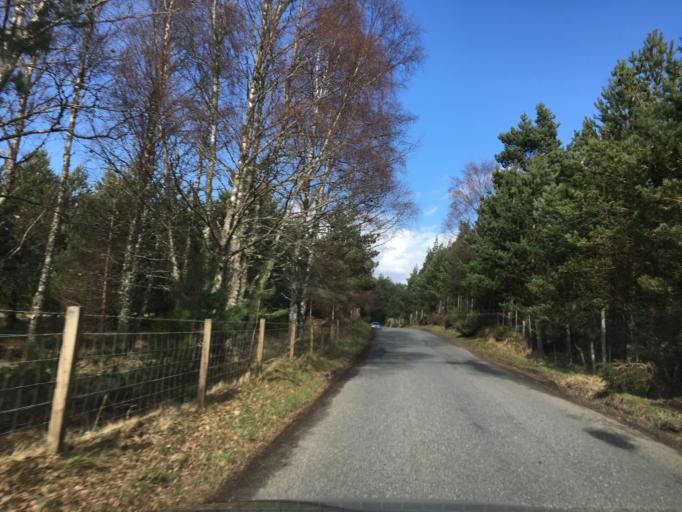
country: GB
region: Scotland
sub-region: Highland
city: Aviemore
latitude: 57.1939
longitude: -3.7994
